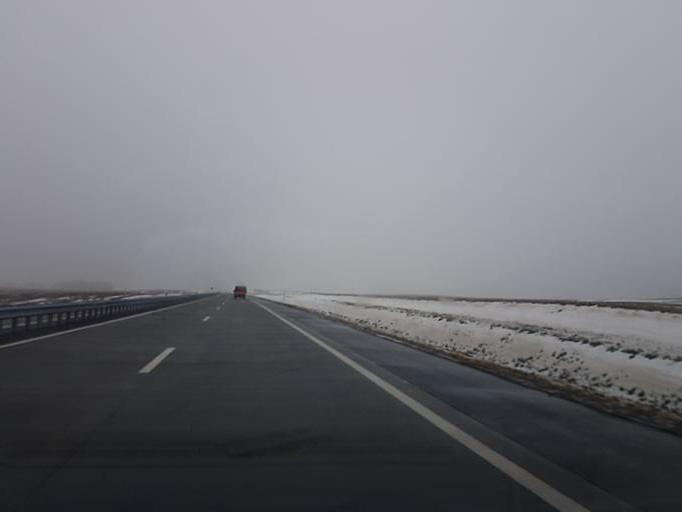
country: BY
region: Minsk
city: Atolina
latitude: 53.7464
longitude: 27.4148
